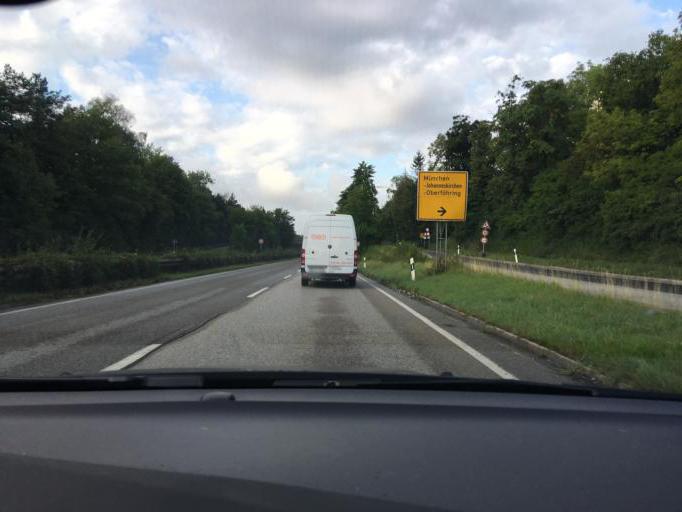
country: DE
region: Bavaria
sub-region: Upper Bavaria
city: Unterfoehring
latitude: 48.1721
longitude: 11.6325
